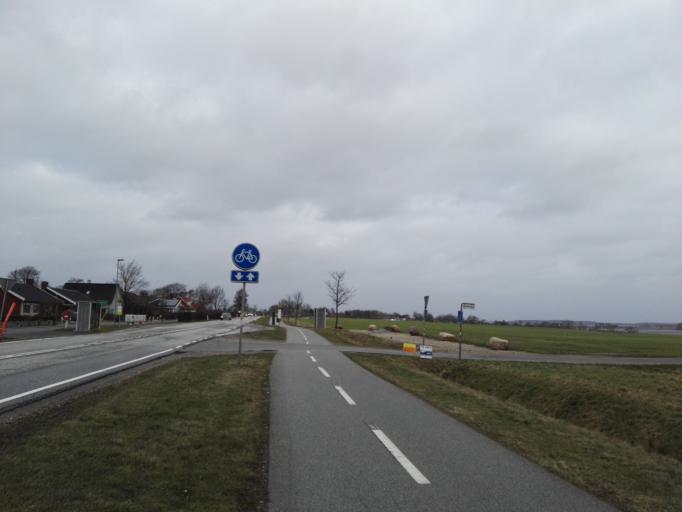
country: DK
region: Zealand
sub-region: Lejre Kommune
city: Lejre
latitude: 55.6614
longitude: 11.9222
